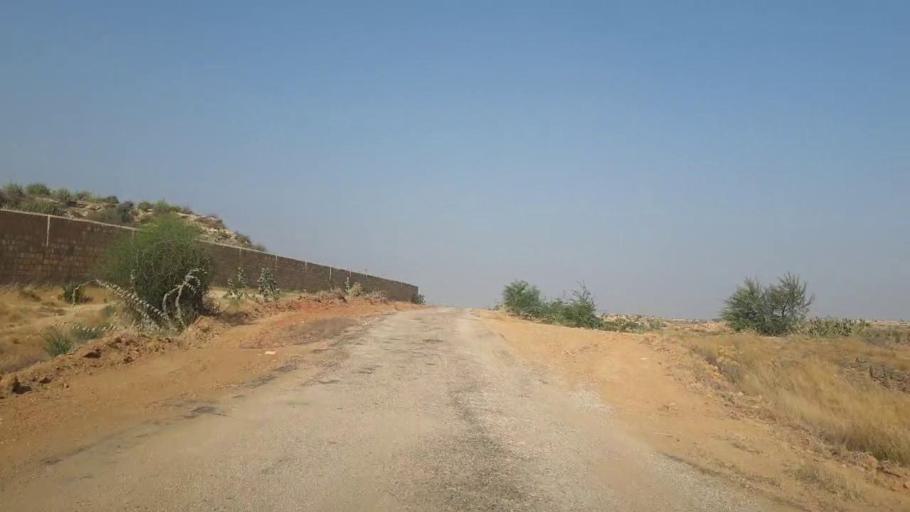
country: PK
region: Sindh
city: Gharo
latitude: 25.0497
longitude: 67.5441
